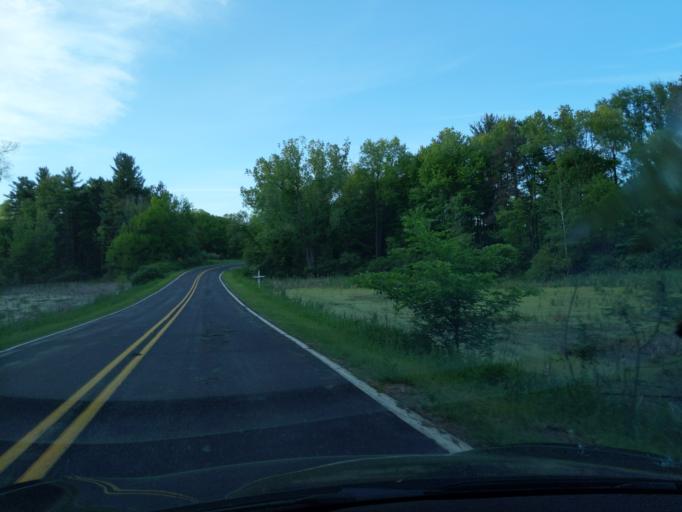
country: US
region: Michigan
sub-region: Ingham County
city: Leslie
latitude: 42.5078
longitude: -84.3121
